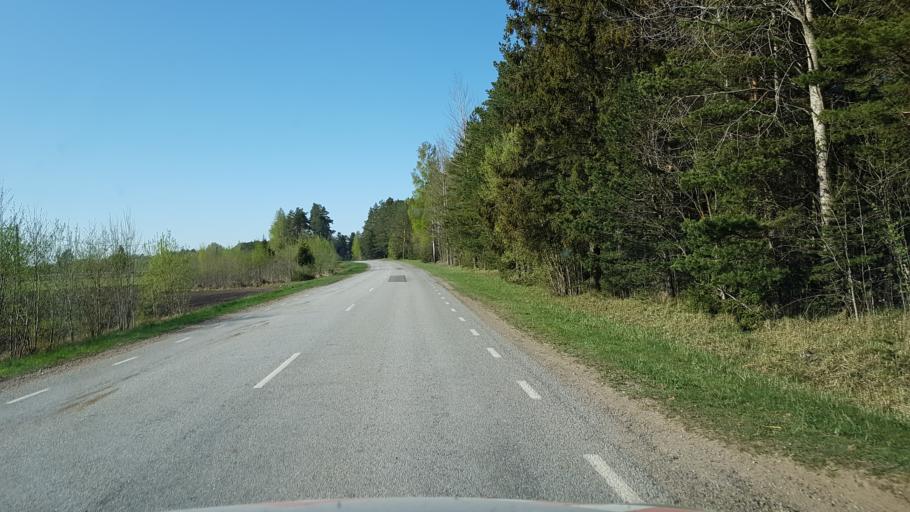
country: EE
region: Paernumaa
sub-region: Paikuse vald
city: Paikuse
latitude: 58.3512
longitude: 24.6663
